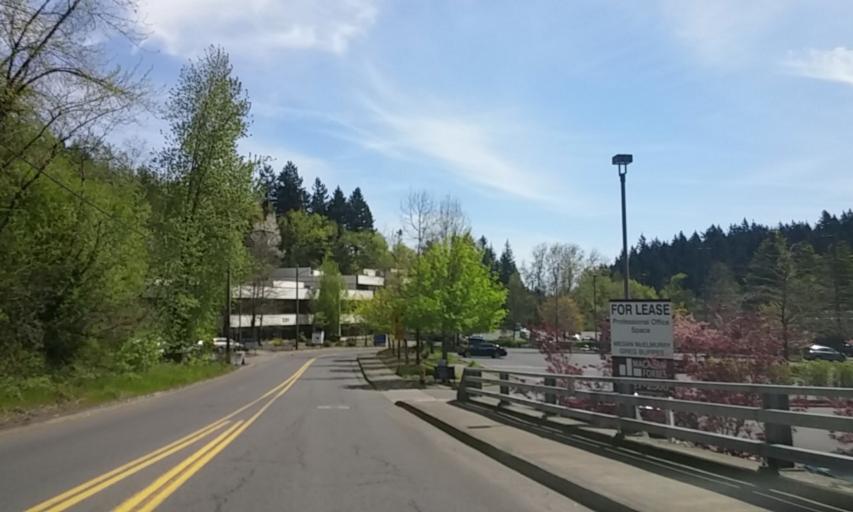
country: US
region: Oregon
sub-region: Washington County
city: West Slope
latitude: 45.5107
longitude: -122.7333
